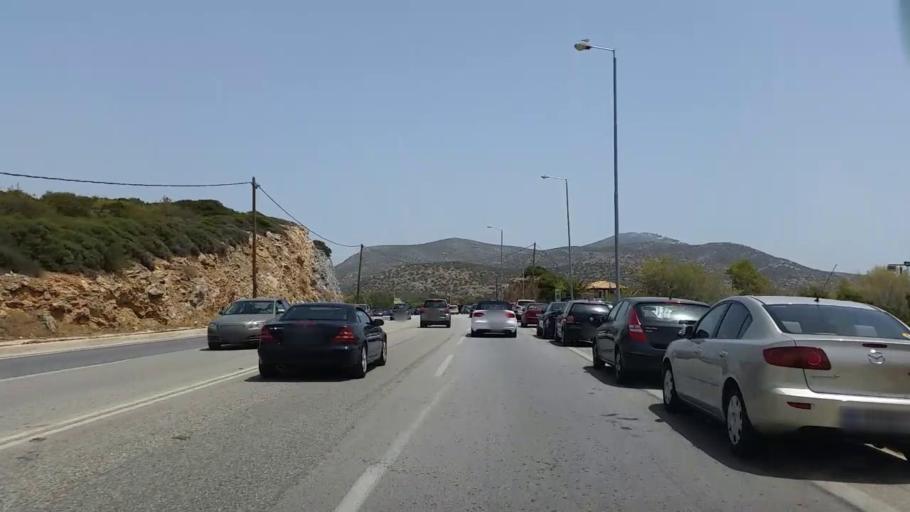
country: GR
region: Attica
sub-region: Nomarchia Anatolikis Attikis
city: Saronida
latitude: 37.7793
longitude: 23.8931
